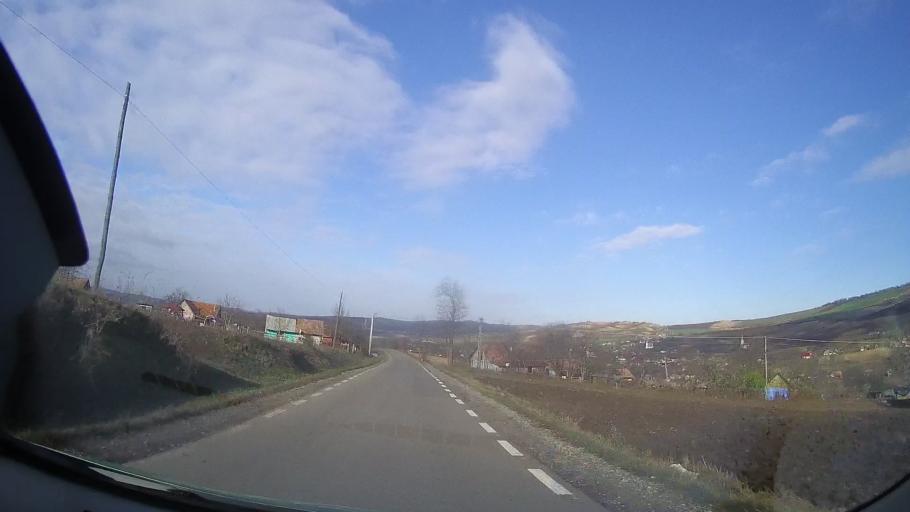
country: RO
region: Mures
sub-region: Comuna Sanger
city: Sanger
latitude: 46.5503
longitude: 24.1452
